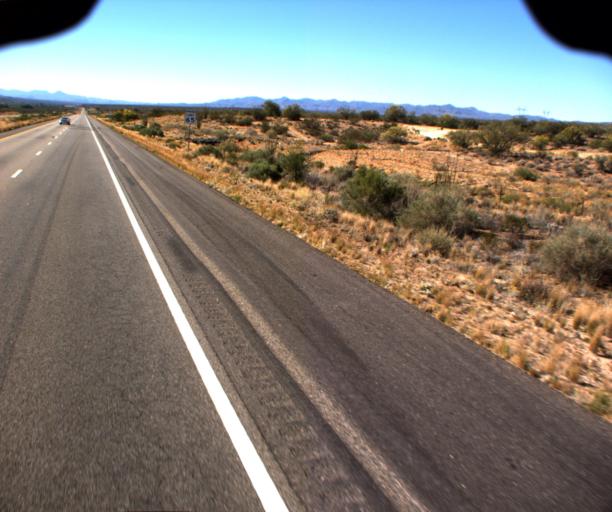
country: US
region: Arizona
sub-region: Mohave County
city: Kingman
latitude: 34.8685
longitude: -113.6442
